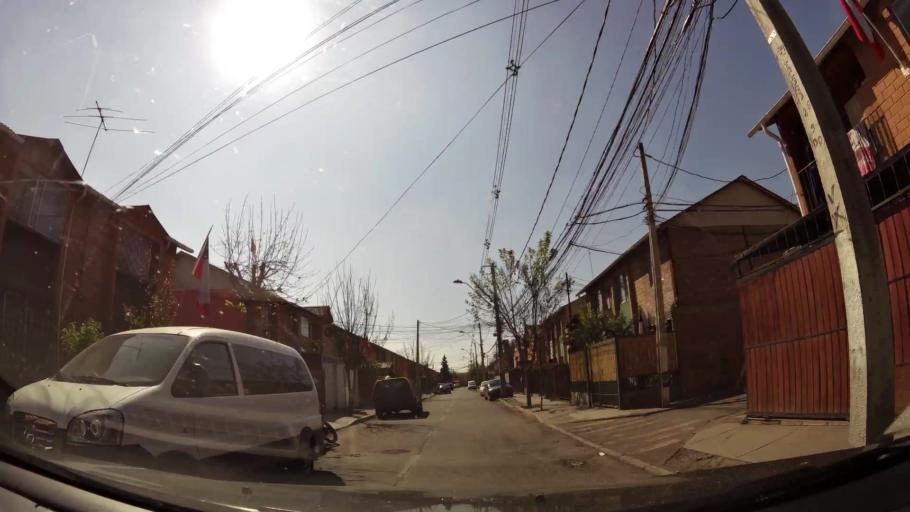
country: CL
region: Santiago Metropolitan
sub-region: Provincia de Santiago
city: Lo Prado
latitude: -33.3591
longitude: -70.7447
